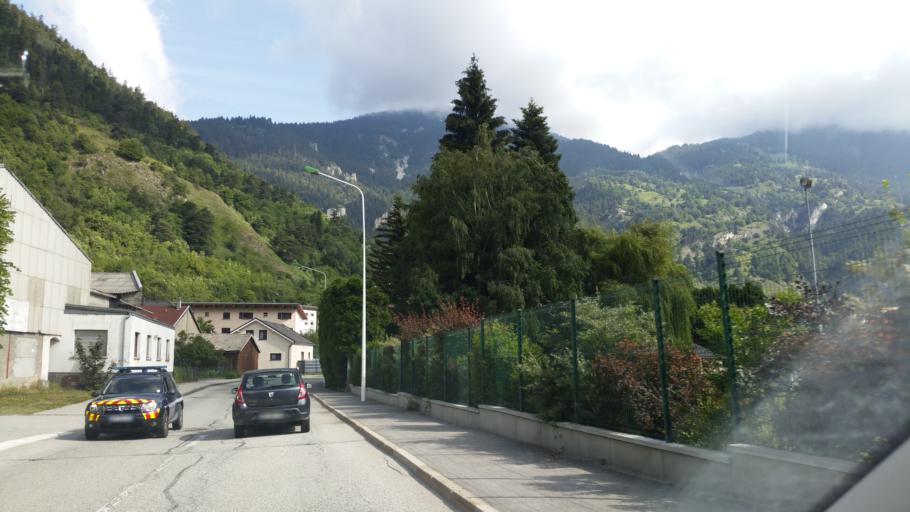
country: FR
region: Rhone-Alpes
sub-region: Departement de la Savoie
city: Modane
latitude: 45.1989
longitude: 6.6644
